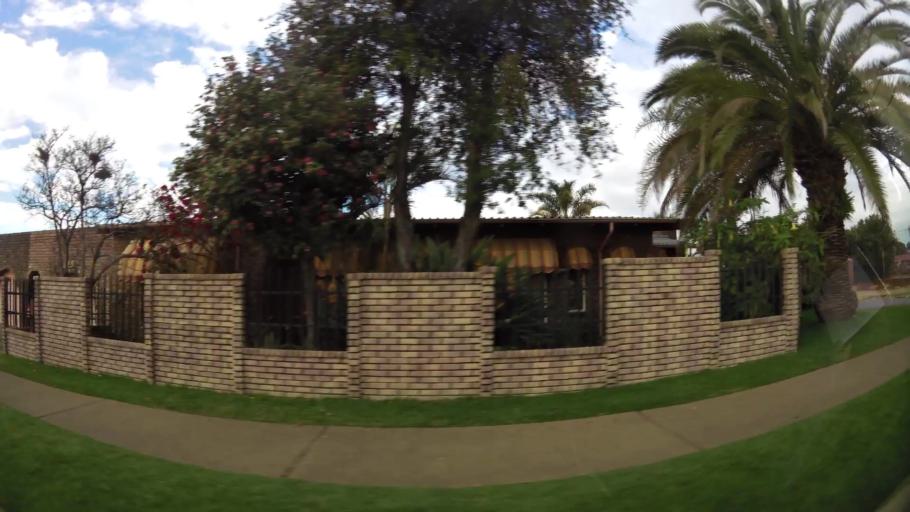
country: ZA
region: Gauteng
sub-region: City of Tshwane Metropolitan Municipality
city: Pretoria
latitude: -25.7129
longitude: 28.3082
